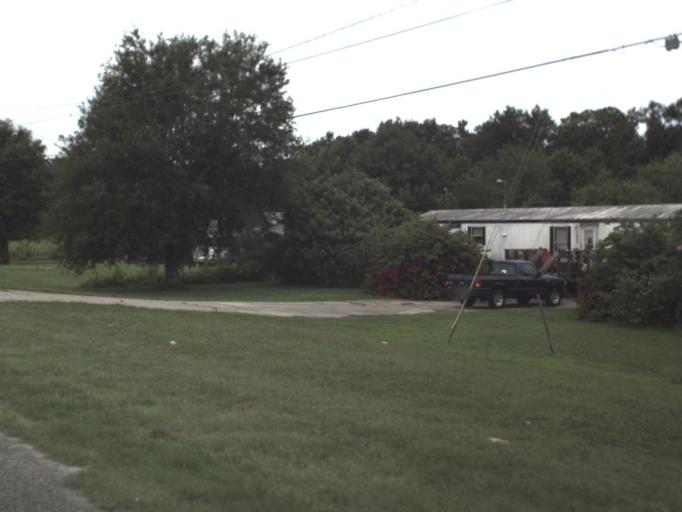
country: US
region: Florida
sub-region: Polk County
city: Eagle Lake
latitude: 27.9418
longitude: -81.8022
